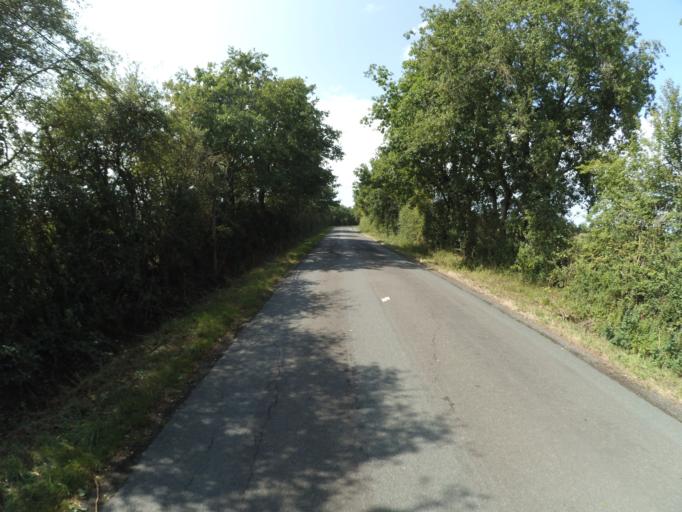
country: FR
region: Pays de la Loire
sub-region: Departement de la Vendee
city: La Bruffiere
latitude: 47.0222
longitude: -1.2229
